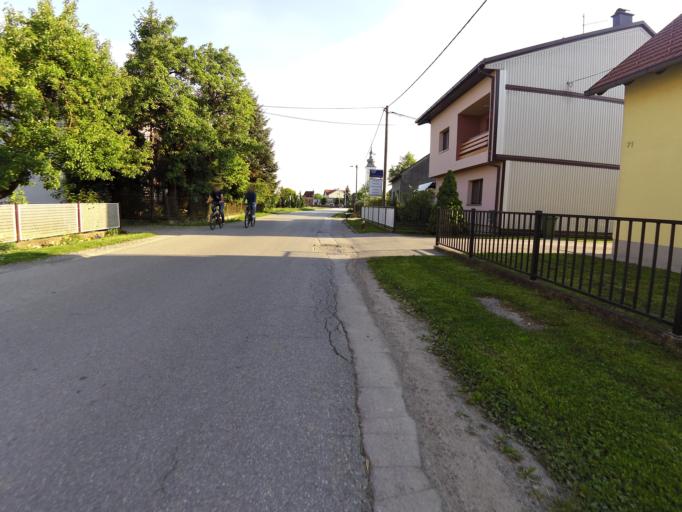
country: HR
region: Karlovacka
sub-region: Grad Karlovac
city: Karlovac
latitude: 45.5215
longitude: 15.5313
